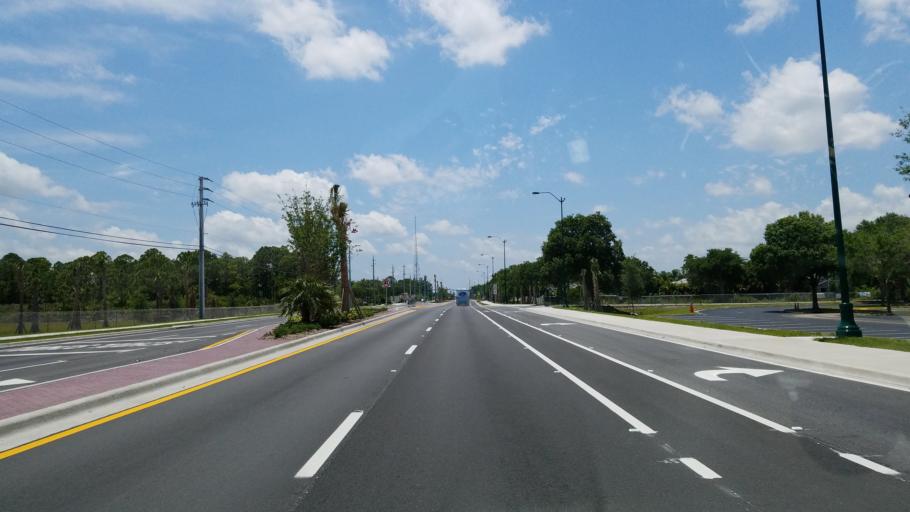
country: US
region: Florida
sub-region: Martin County
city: Palm City
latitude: 27.1614
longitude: -80.2920
